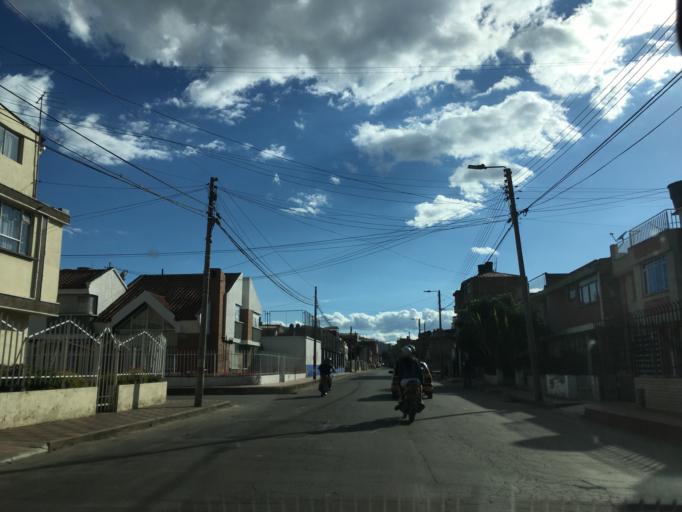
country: CO
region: Boyaca
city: Sogamoso
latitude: 5.7239
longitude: -72.9245
